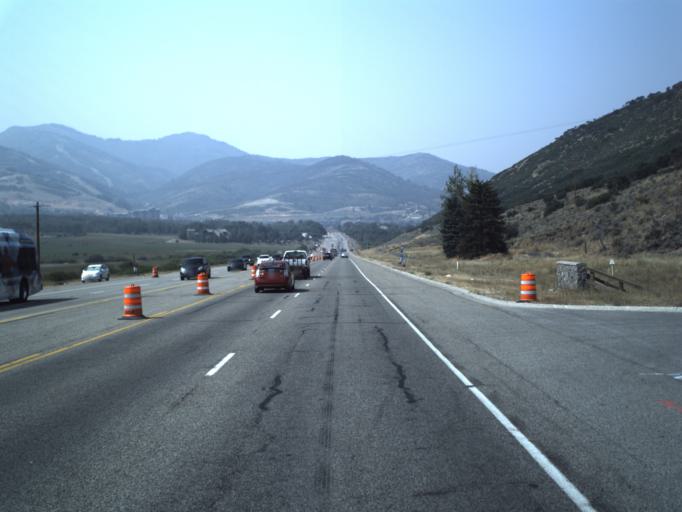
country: US
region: Utah
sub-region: Summit County
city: Snyderville
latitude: 40.6781
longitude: -111.5256
